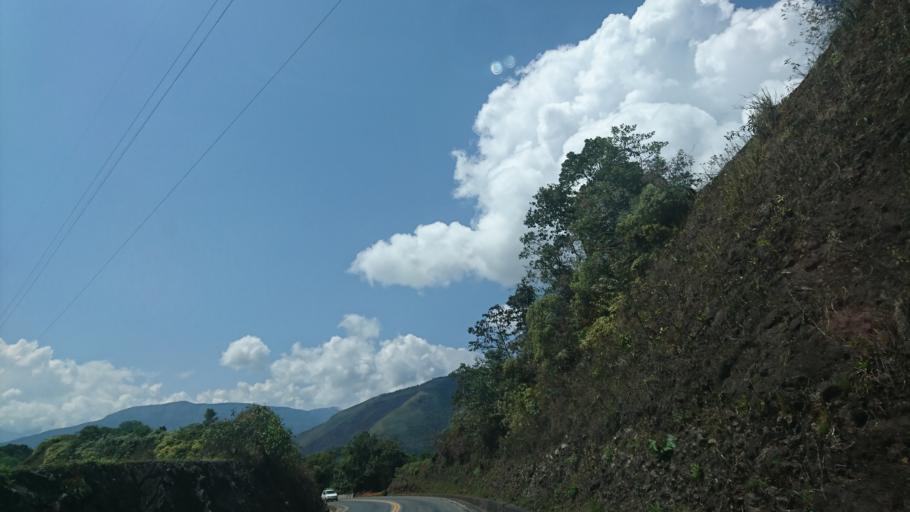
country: BO
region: La Paz
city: Coroico
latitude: -16.2140
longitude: -67.7912
